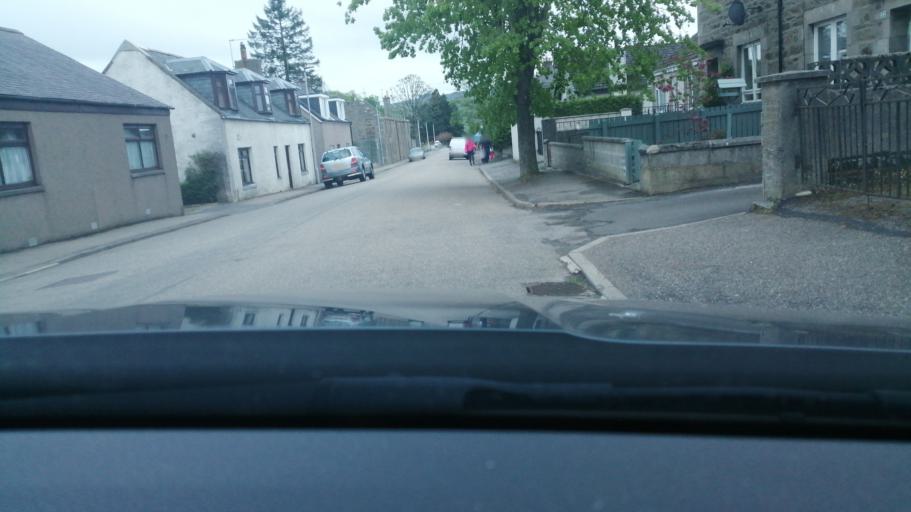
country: GB
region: Scotland
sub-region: Moray
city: Keith
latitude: 57.5377
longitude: -2.9478
